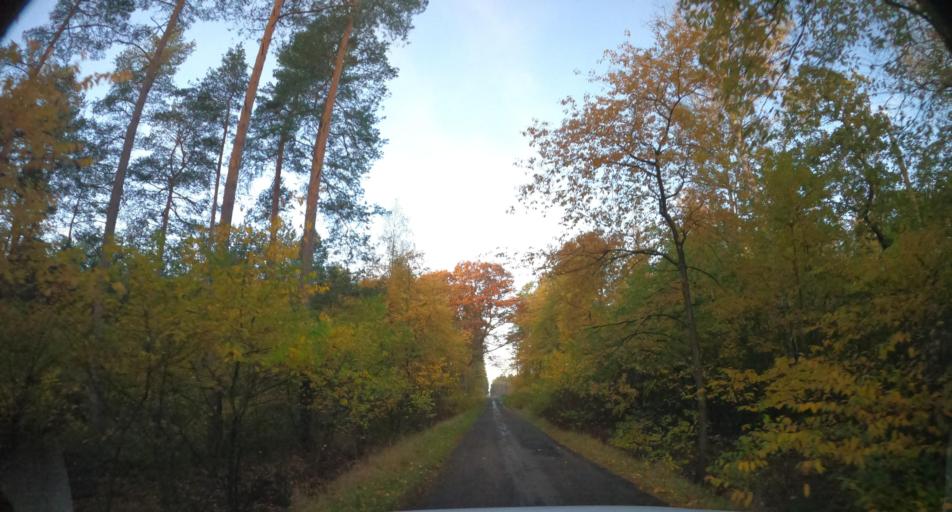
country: PL
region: West Pomeranian Voivodeship
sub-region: Powiat policki
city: Nowe Warpno
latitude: 53.6431
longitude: 14.3668
